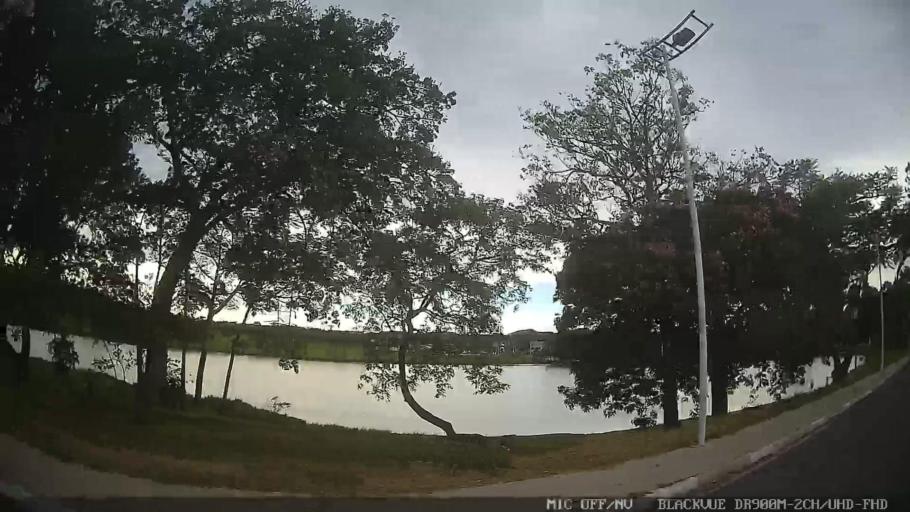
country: BR
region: Sao Paulo
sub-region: Atibaia
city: Atibaia
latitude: -23.1115
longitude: -46.5228
